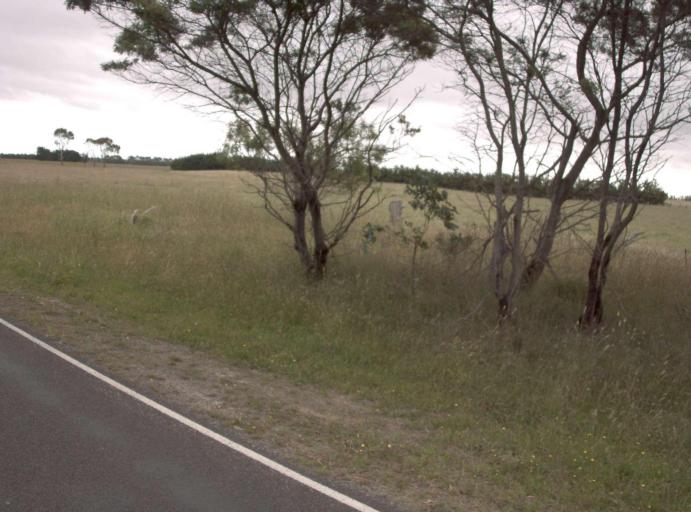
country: AU
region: Victoria
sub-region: Wellington
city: Sale
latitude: -38.5367
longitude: 146.8888
